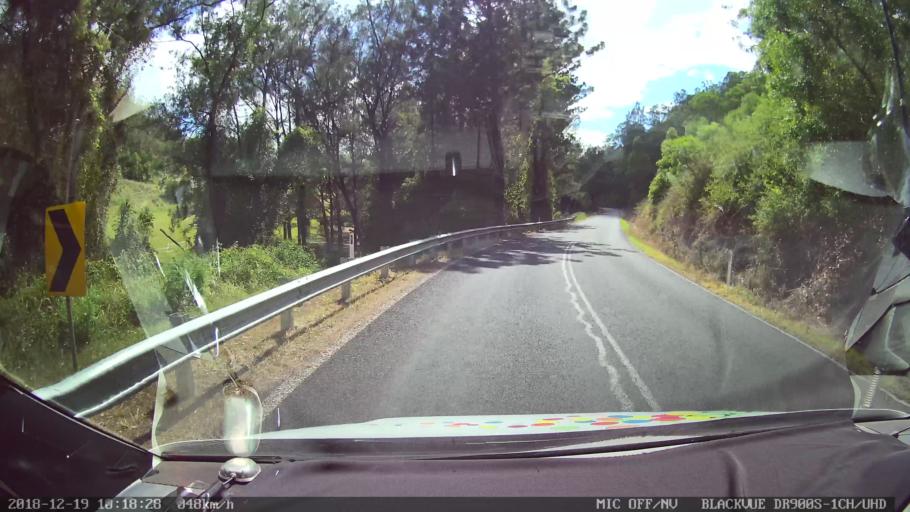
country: AU
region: New South Wales
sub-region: Kyogle
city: Kyogle
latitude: -28.6013
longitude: 153.0388
